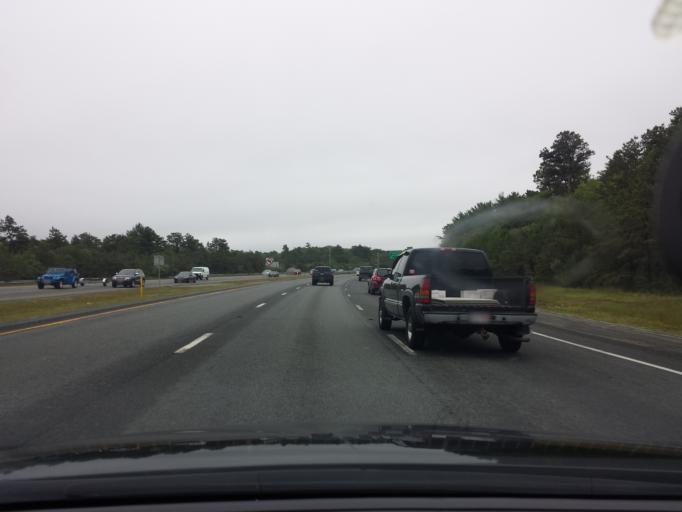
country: US
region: Massachusetts
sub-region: Barnstable County
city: Bourne
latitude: 41.7730
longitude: -70.5862
